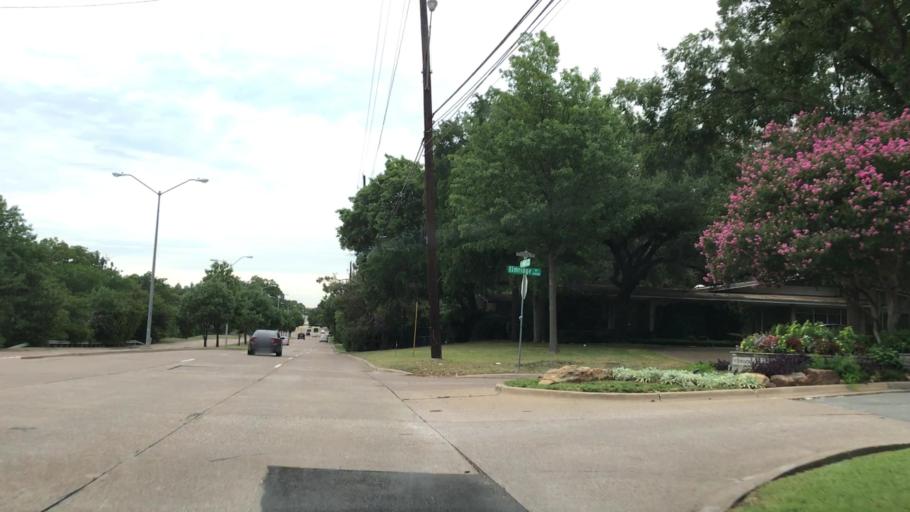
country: US
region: Texas
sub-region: Dallas County
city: Addison
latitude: 32.9345
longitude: -96.7861
